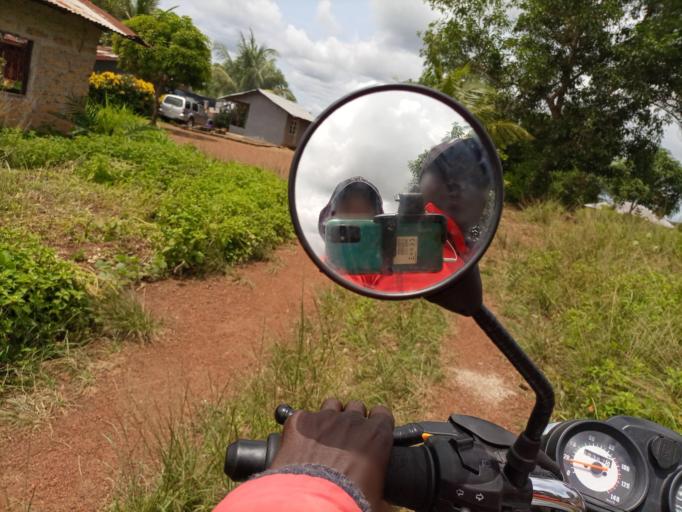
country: SL
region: Southern Province
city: Baoma
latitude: 7.9735
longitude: -11.7125
